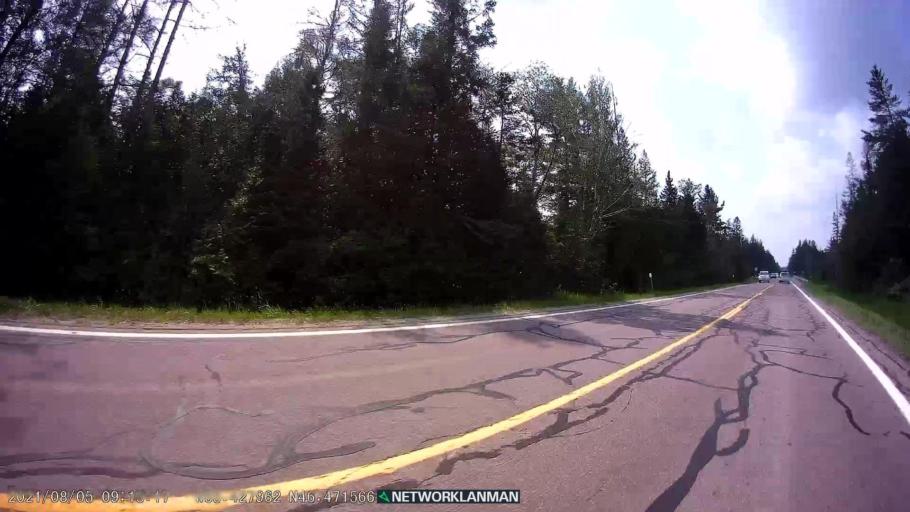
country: US
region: Michigan
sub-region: Luce County
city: Newberry
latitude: 46.4713
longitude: -85.4280
